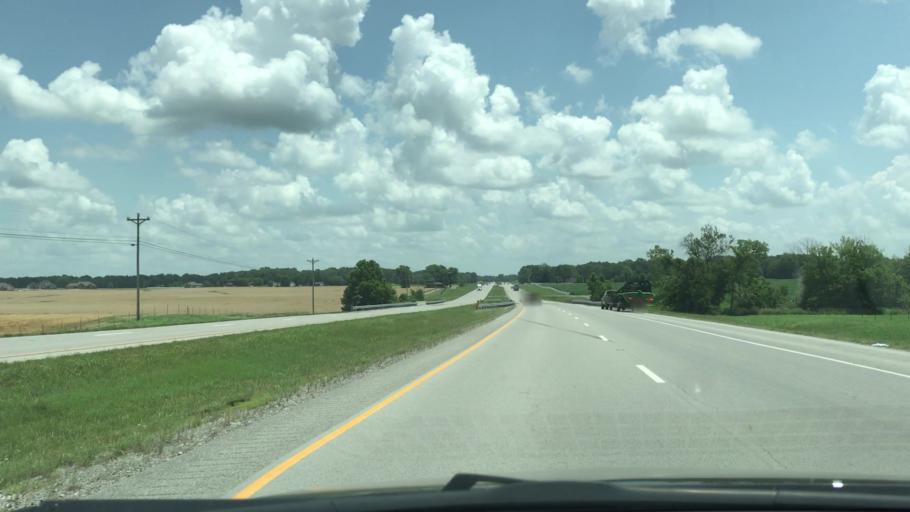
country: US
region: Kentucky
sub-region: Christian County
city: Hopkinsville
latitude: 36.8803
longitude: -87.5917
